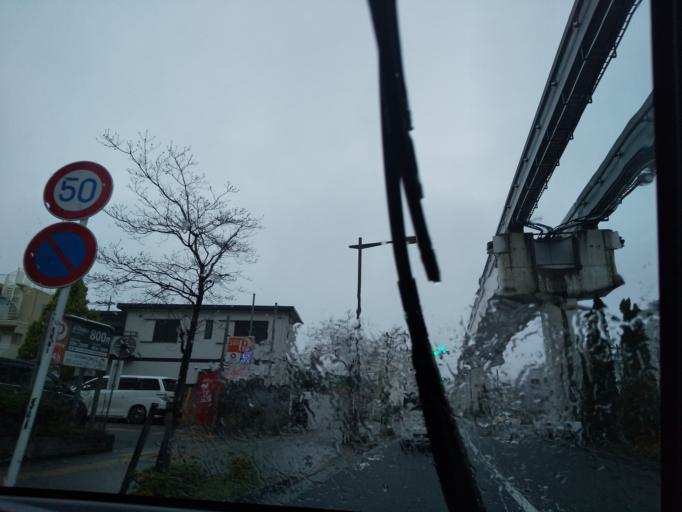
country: JP
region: Tokyo
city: Hino
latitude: 35.6913
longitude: 139.4099
